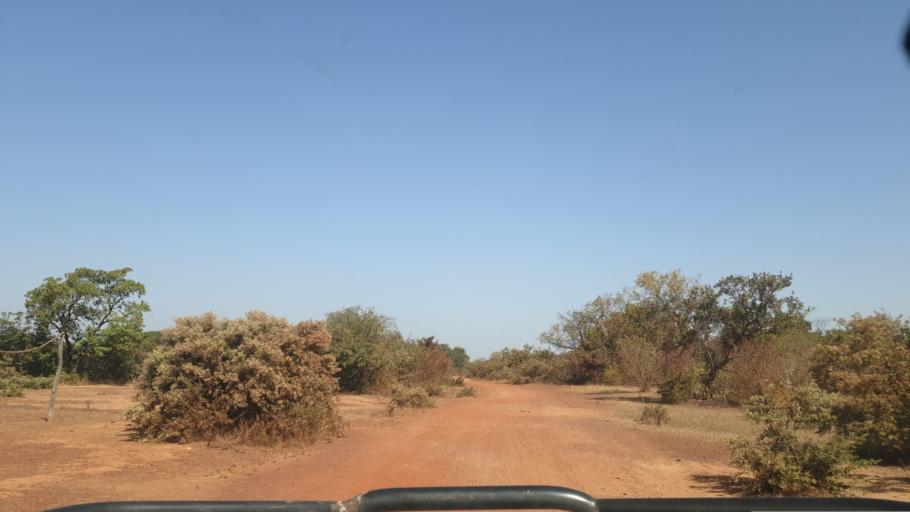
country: ML
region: Sikasso
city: Bougouni
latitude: 11.8307
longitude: -6.9787
